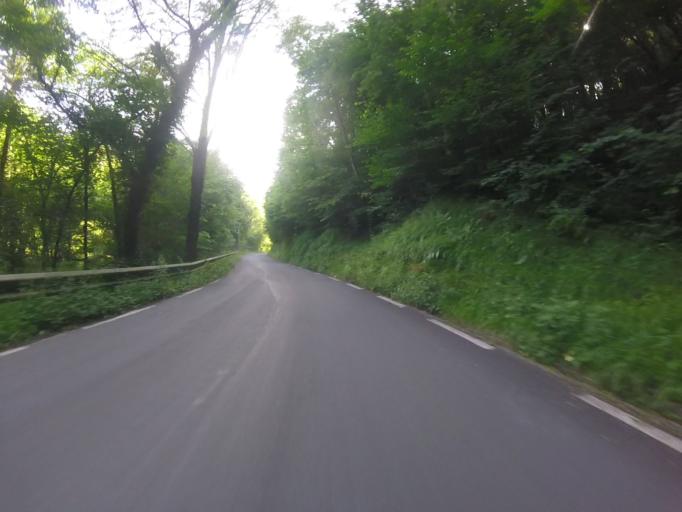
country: ES
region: Basque Country
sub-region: Provincia de Guipuzcoa
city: Beasain
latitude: 43.0743
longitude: -2.2270
